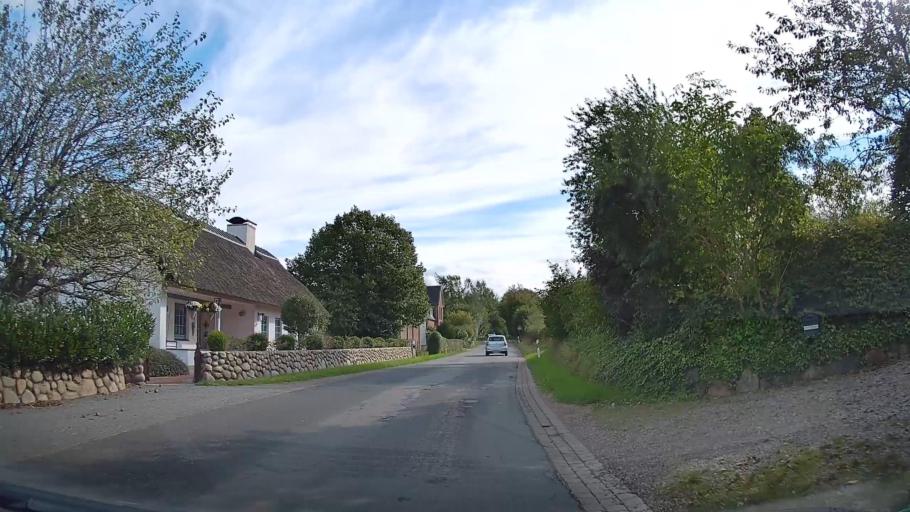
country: DE
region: Schleswig-Holstein
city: Ringsberg
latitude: 54.8399
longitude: 9.5872
